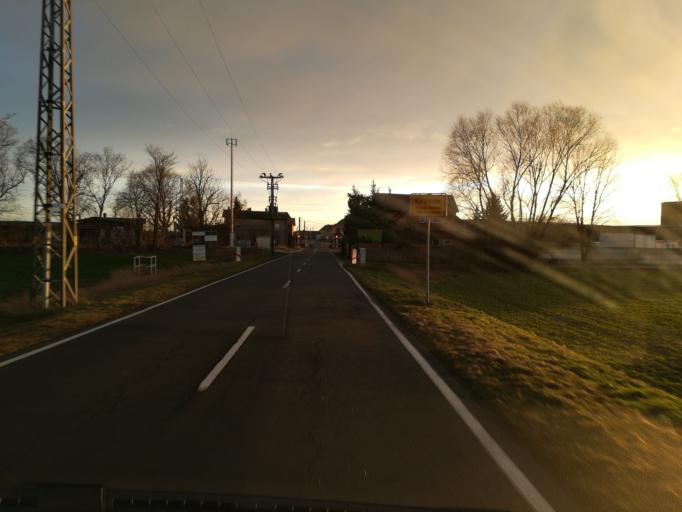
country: DE
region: Saxony-Anhalt
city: Brehna
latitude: 51.5093
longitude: 12.2282
